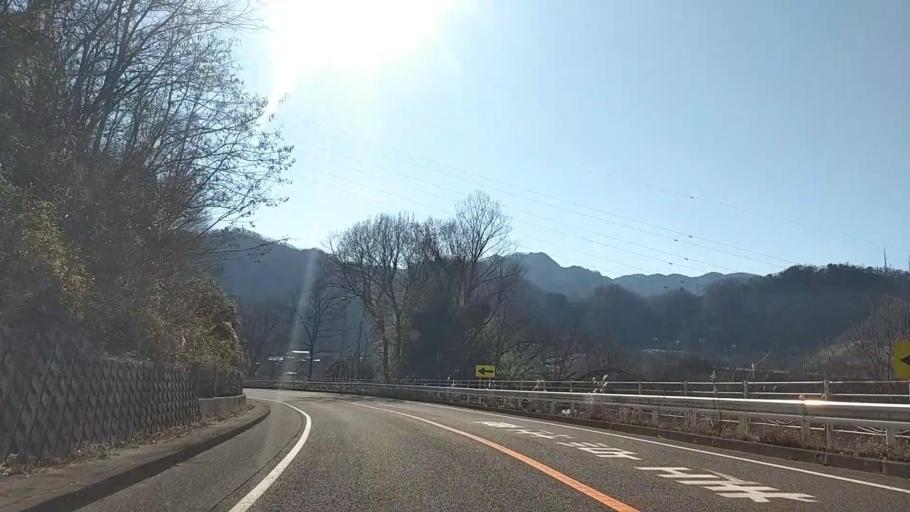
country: JP
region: Yamanashi
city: Uenohara
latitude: 35.6274
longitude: 139.1036
